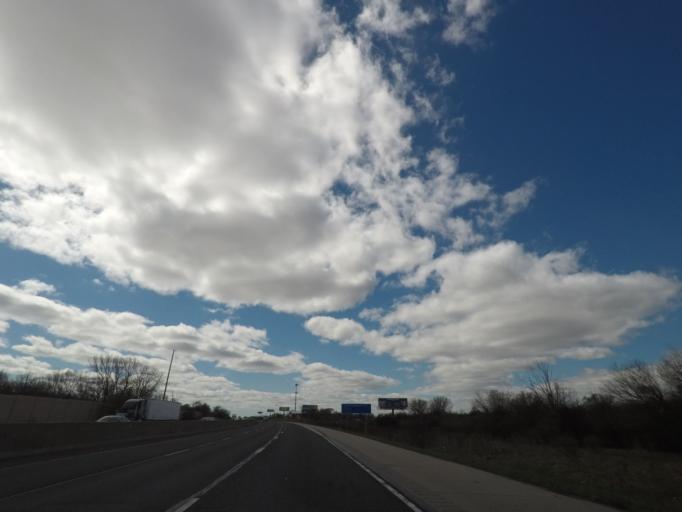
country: US
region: Illinois
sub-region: Will County
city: Plainfield
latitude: 41.6309
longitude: -88.1635
